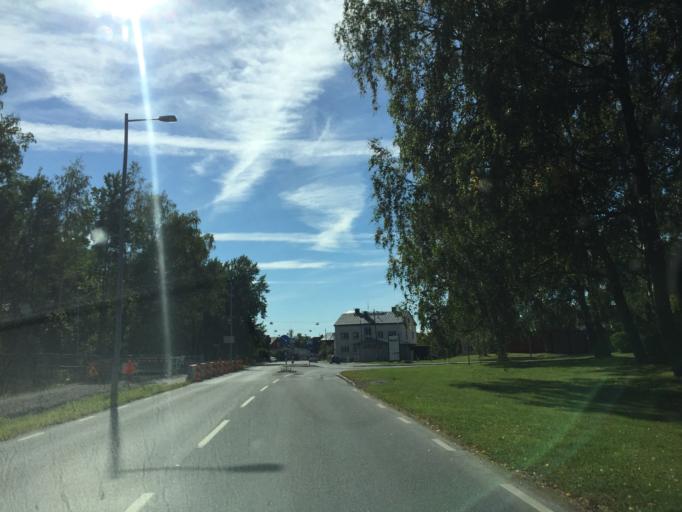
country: SE
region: OErebro
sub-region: Orebro Kommun
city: Orebro
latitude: 59.2860
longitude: 15.2374
